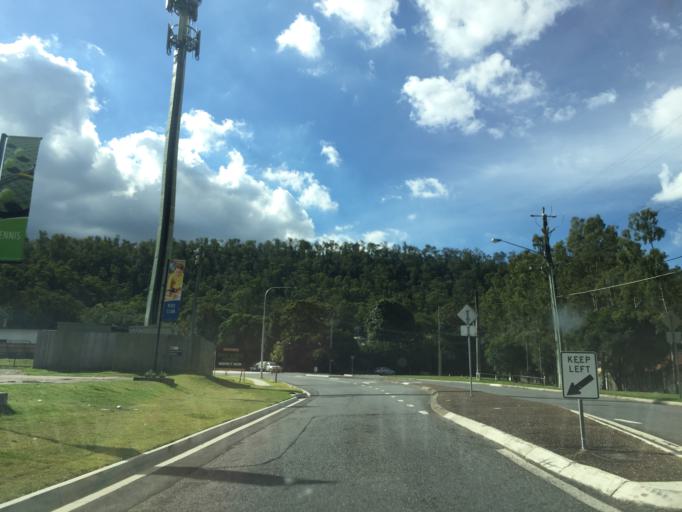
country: AU
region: Queensland
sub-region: Moreton Bay
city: Ferny Hills
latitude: -27.4309
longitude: 152.9433
